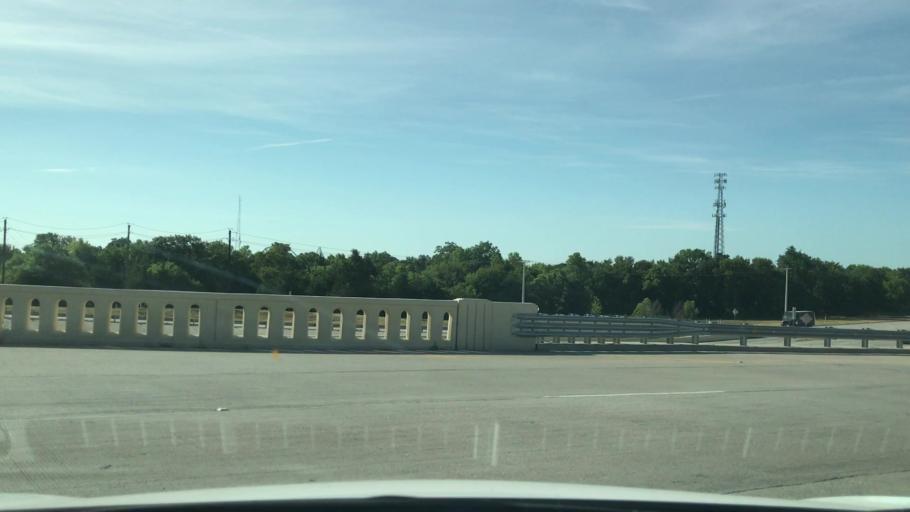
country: US
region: Texas
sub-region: Collin County
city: McKinney
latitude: 33.2396
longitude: -96.6306
